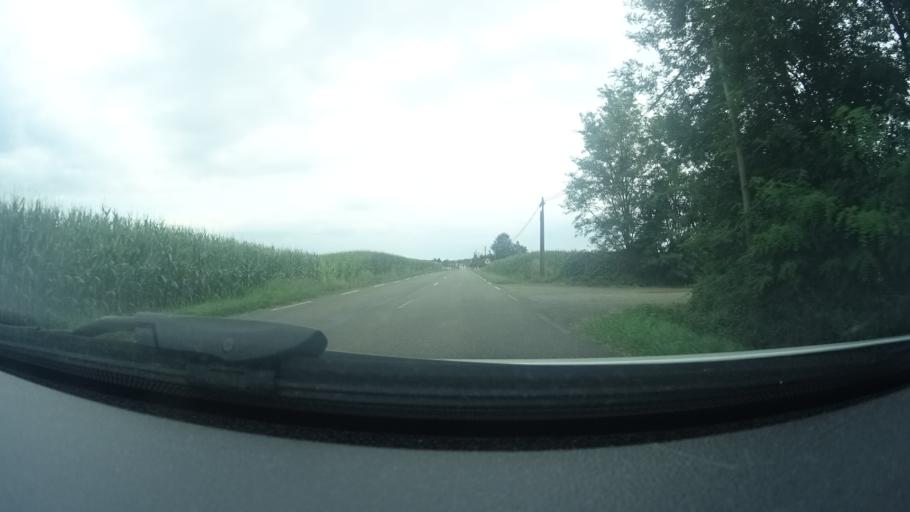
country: FR
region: Aquitaine
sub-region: Departement des Pyrenees-Atlantiques
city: Mont
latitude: 43.4480
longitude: -0.7014
